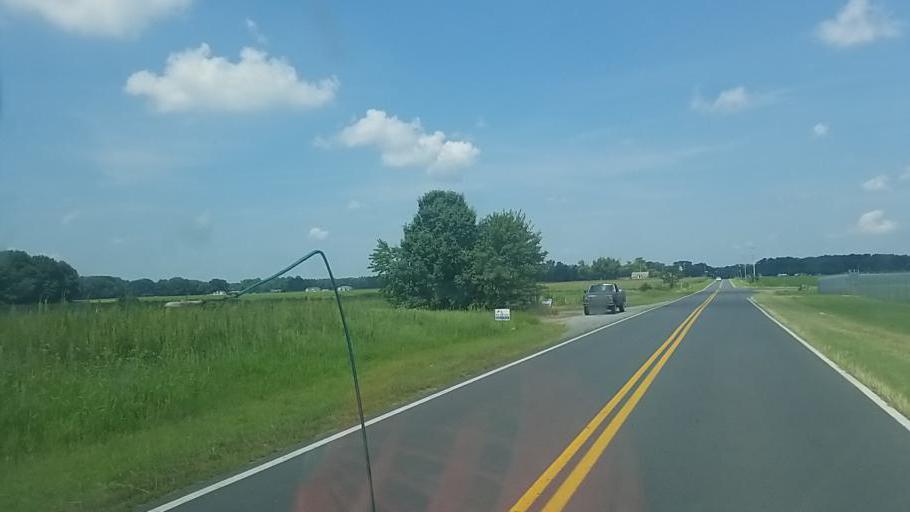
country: US
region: Maryland
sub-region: Wicomico County
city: Salisbury
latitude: 38.3464
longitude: -75.5201
